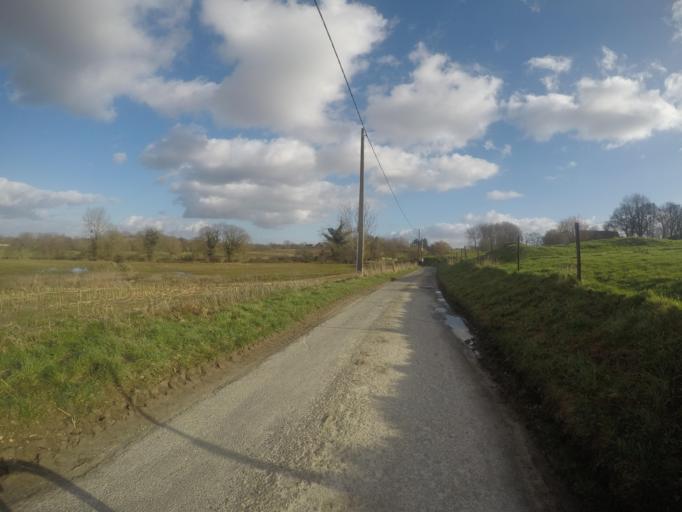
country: BE
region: Wallonia
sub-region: Province du Brabant Wallon
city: Rebecq-Rognon
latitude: 50.6447
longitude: 4.0858
